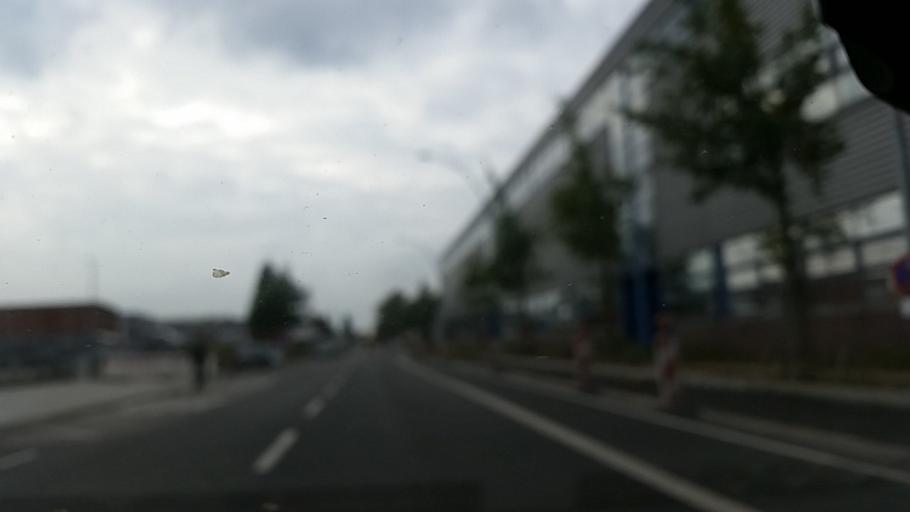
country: DE
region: Hamburg
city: Marienthal
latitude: 53.5338
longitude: 10.0895
